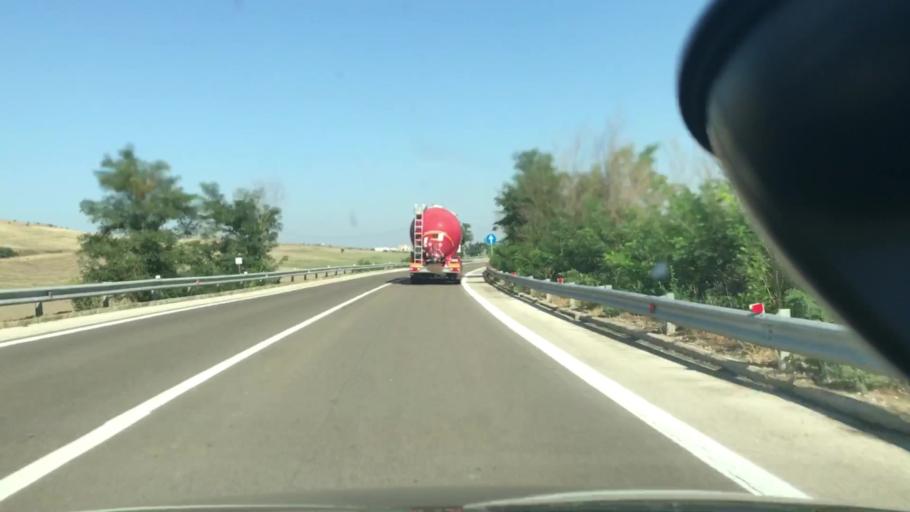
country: IT
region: Basilicate
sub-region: Provincia di Matera
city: Irsina
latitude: 40.7945
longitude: 16.2773
